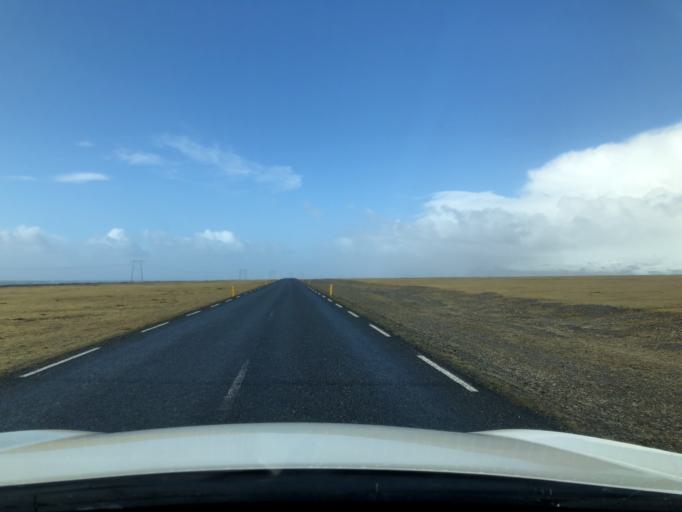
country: IS
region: East
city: Hoefn
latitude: 64.0596
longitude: -16.1459
